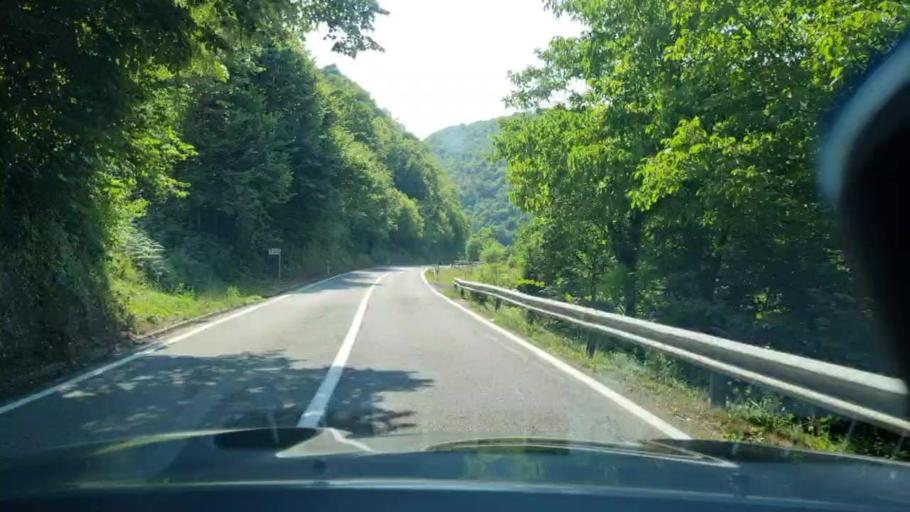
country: BA
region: Federation of Bosnia and Herzegovina
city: Bosanska Krupa
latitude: 44.8779
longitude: 16.1238
